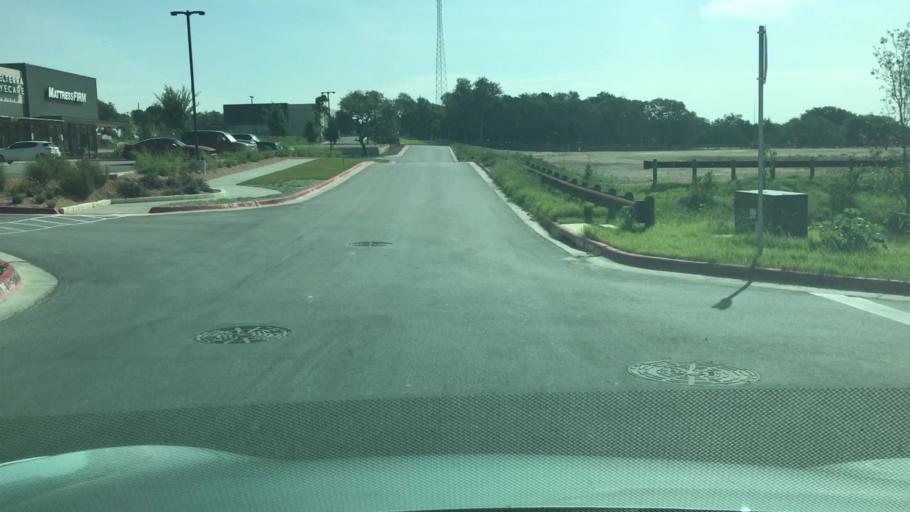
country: US
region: Texas
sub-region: Travis County
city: Bee Cave
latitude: 30.2057
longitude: -97.9769
